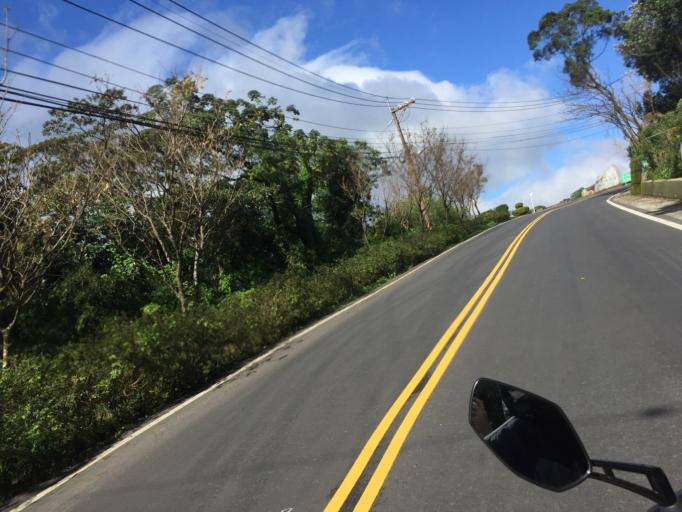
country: TW
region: Taipei
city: Taipei
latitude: 25.2148
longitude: 121.5083
